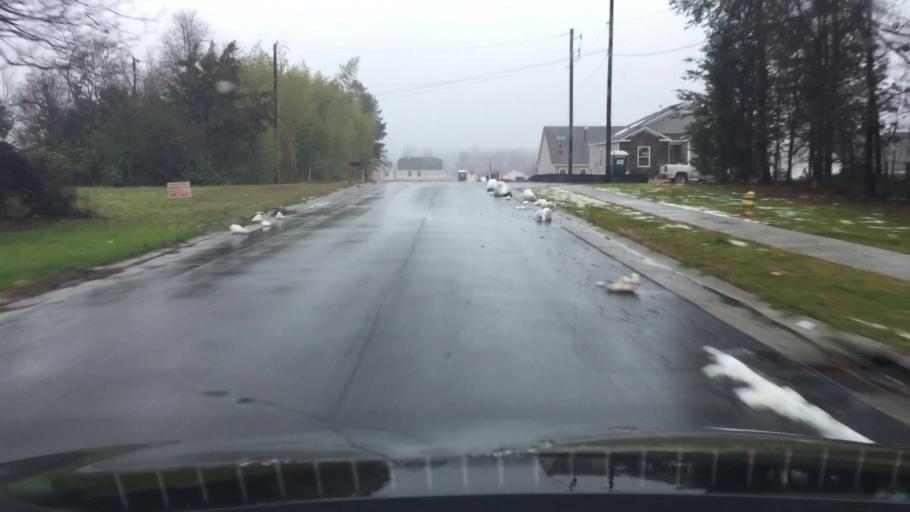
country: US
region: North Carolina
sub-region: Iredell County
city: Mooresville
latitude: 35.5792
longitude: -80.7934
